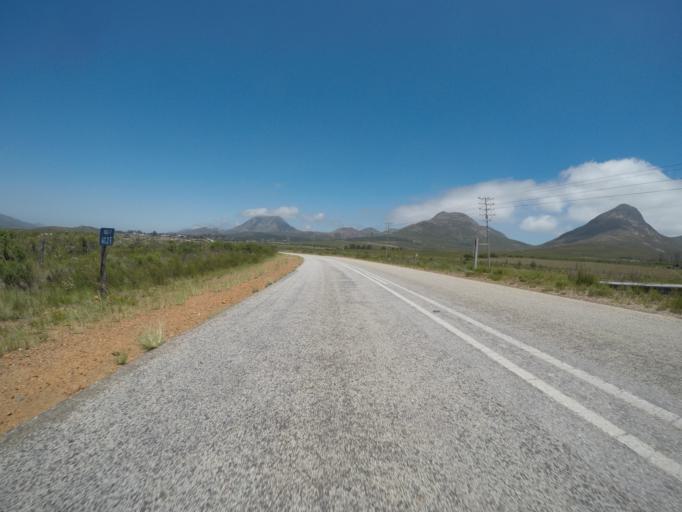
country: ZA
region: Eastern Cape
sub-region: Cacadu District Municipality
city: Kareedouw
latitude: -33.9414
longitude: 24.2667
